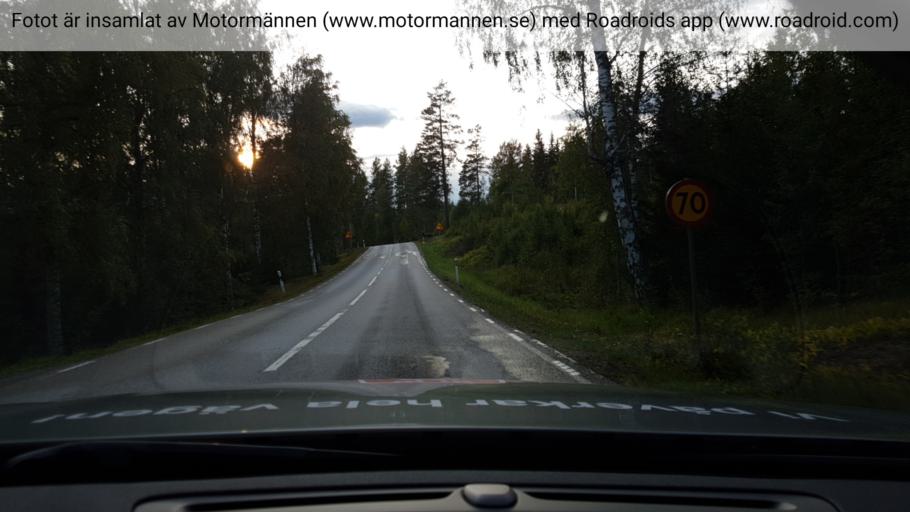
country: SE
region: OErebro
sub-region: Ljusnarsbergs Kommun
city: Kopparberg
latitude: 59.8069
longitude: 14.8445
